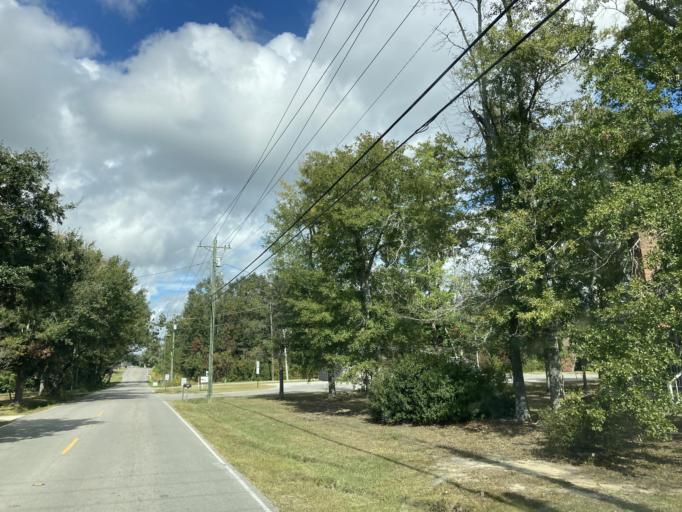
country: US
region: Mississippi
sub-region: Jackson County
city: Gulf Hills
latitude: 30.4475
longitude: -88.8303
